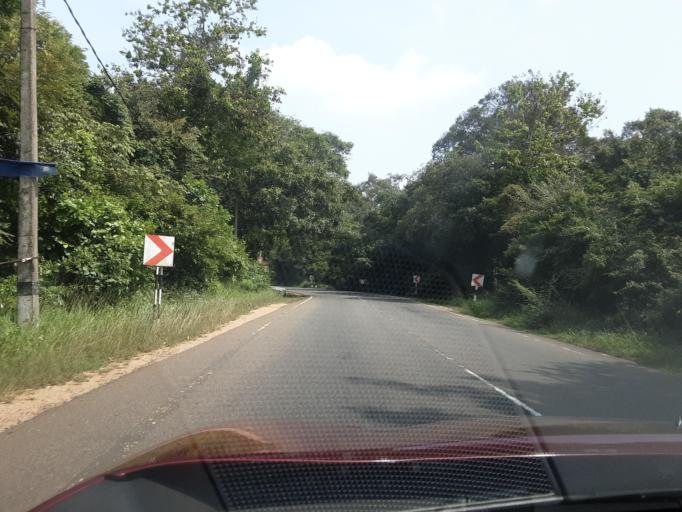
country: LK
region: North Central
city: Anuradhapura
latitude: 8.3464
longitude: 80.5063
